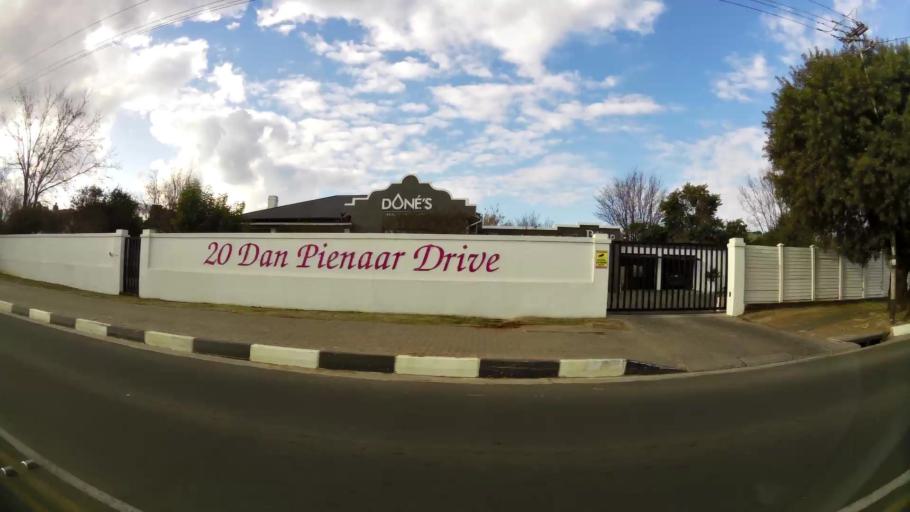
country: ZA
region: Orange Free State
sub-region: Mangaung Metropolitan Municipality
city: Bloemfontein
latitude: -29.0993
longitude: 26.2048
